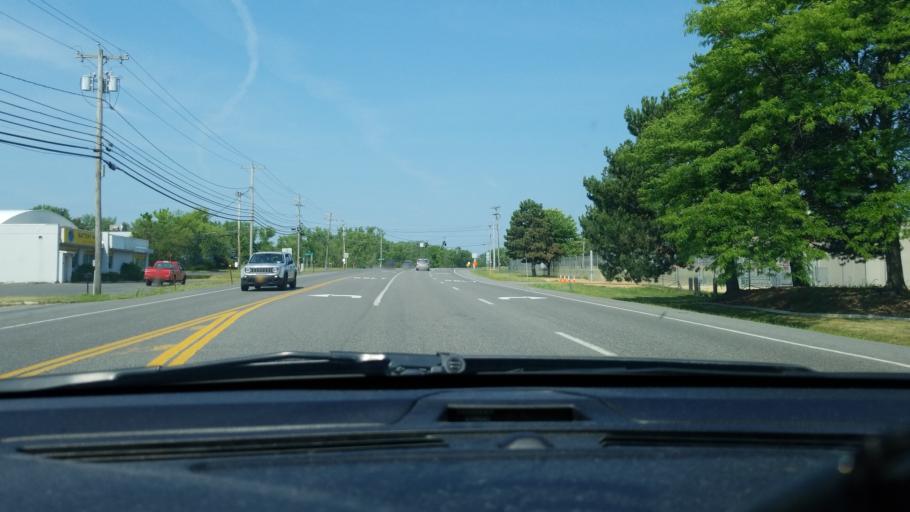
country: US
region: New York
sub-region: Onondaga County
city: Lyncourt
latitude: 43.0984
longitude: -76.1151
